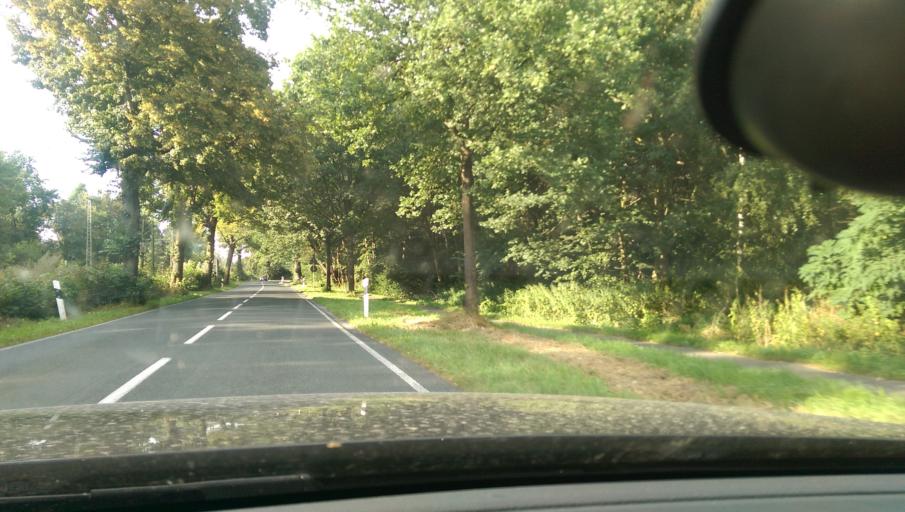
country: DE
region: Lower Saxony
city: Neustadt am Rubenberge
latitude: 52.4749
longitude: 9.4544
